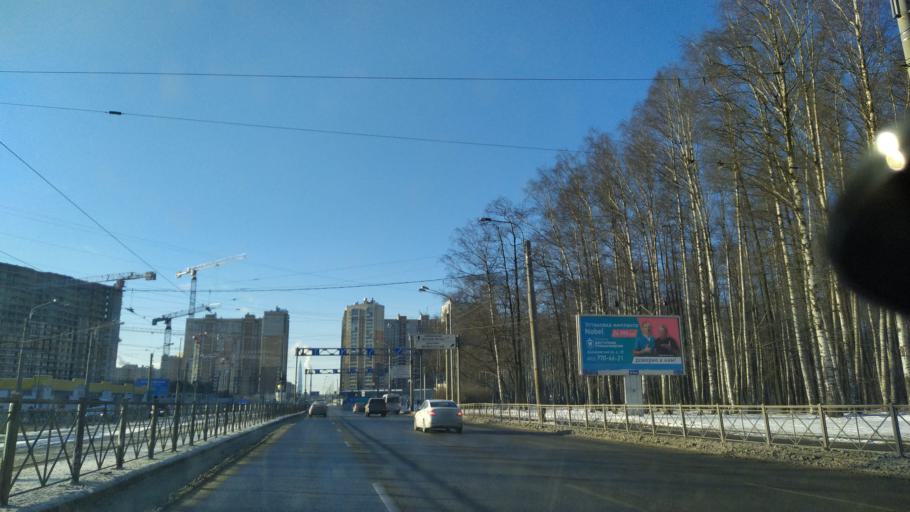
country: RU
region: Leningrad
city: Udel'naya
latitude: 60.0020
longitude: 30.3117
